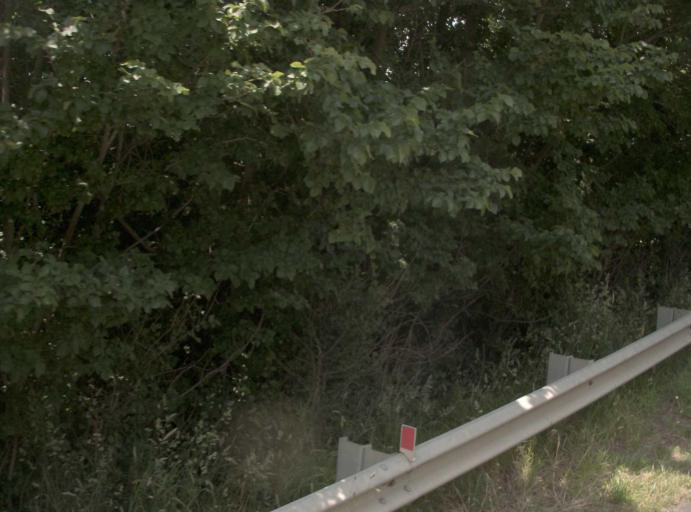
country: AU
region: Victoria
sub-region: Latrobe
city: Traralgon
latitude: -38.3253
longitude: 146.7235
